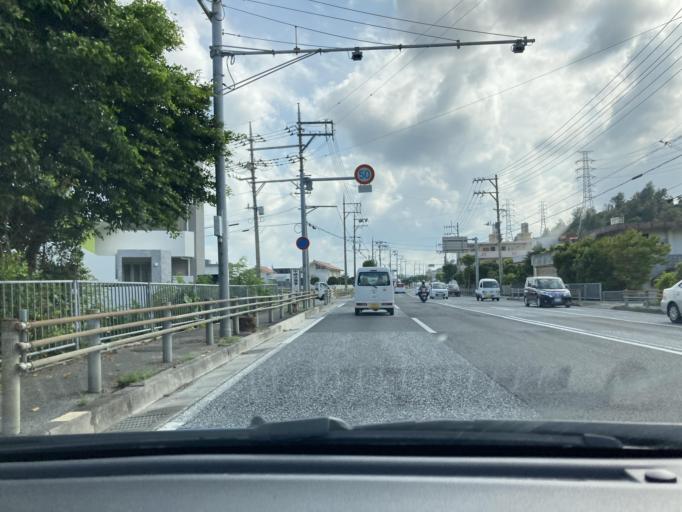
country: JP
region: Okinawa
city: Ginowan
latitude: 26.2552
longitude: 127.7848
